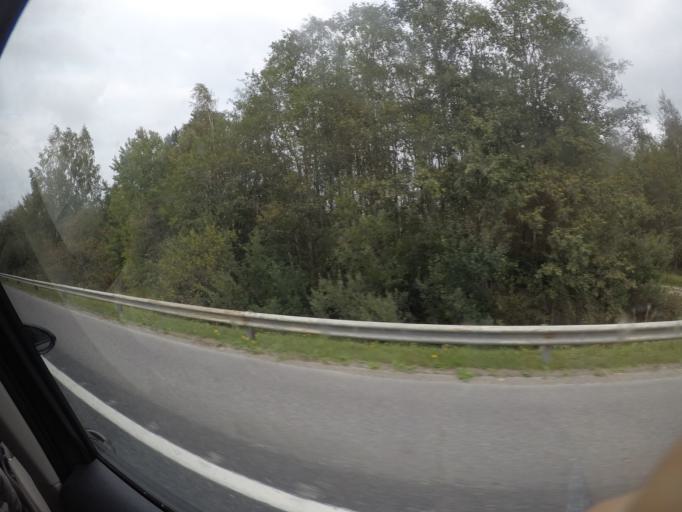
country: FI
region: Haeme
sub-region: Haemeenlinna
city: Parola
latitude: 61.0405
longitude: 24.4028
